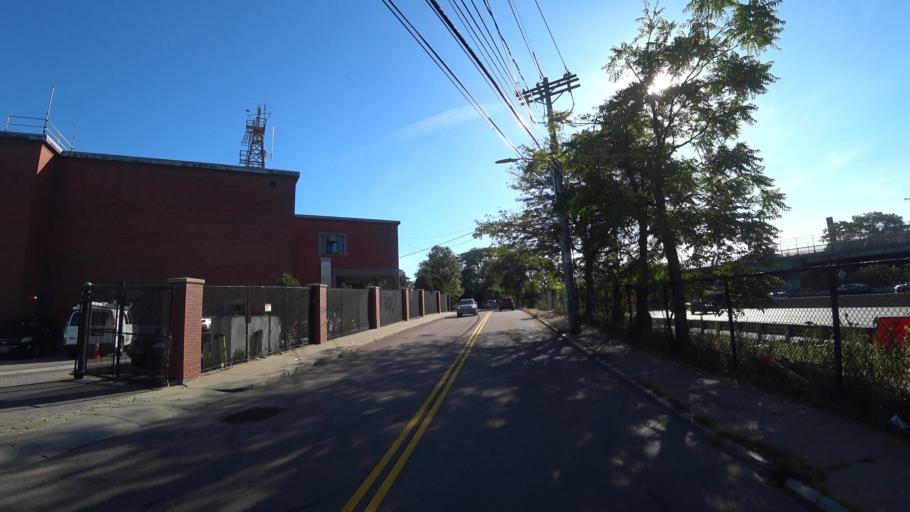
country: US
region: Massachusetts
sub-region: Norfolk County
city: Brookline
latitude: 42.3568
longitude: -71.1318
